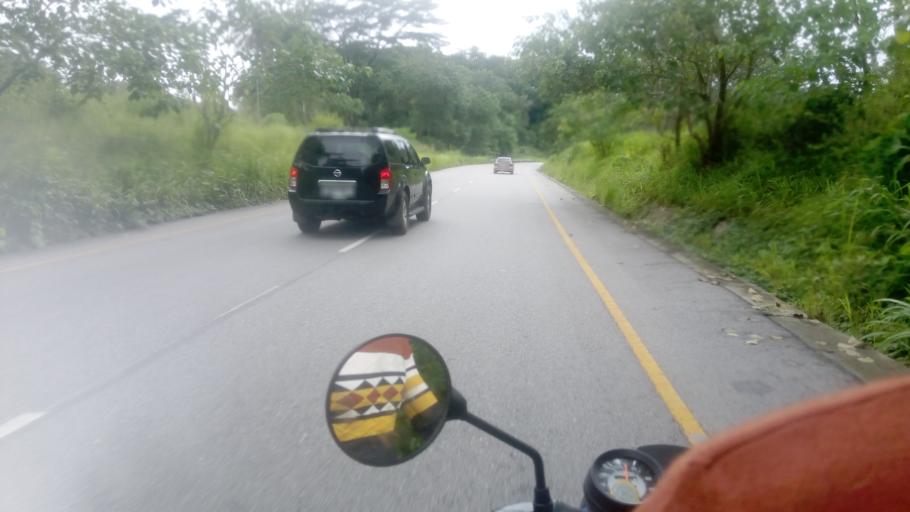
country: SL
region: Northern Province
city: Makali
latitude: 8.6344
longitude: -11.6743
